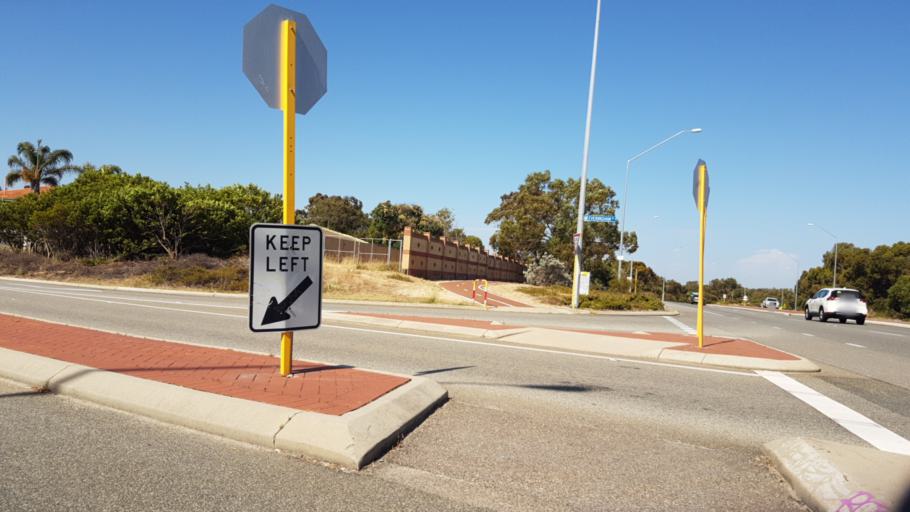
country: AU
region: Western Australia
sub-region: Stirling
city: Karrinyup
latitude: -31.8566
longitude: 115.7775
